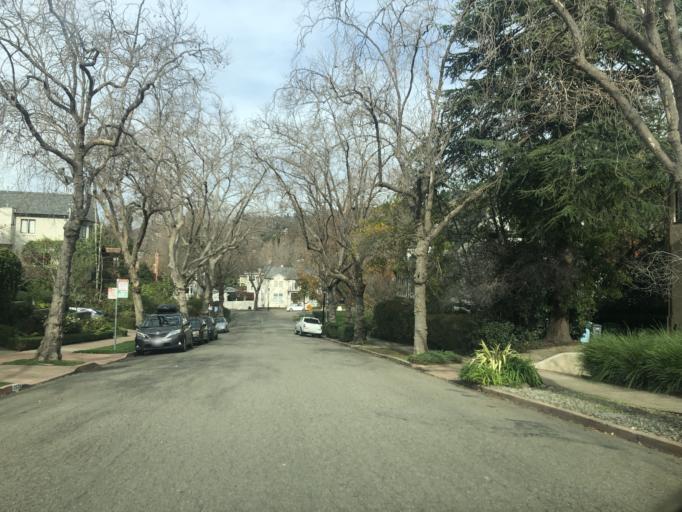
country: US
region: California
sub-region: Alameda County
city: Berkeley
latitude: 37.8599
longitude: -122.2472
